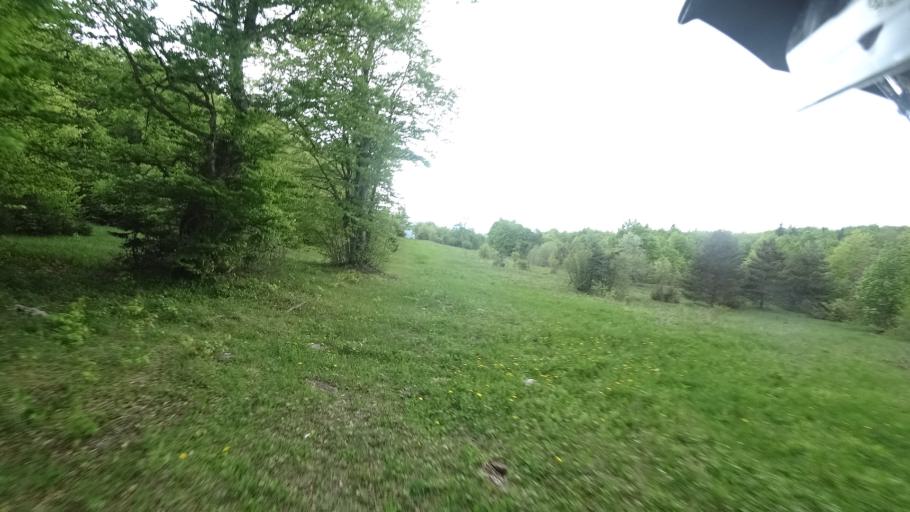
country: HR
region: Karlovacka
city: Plaski
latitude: 44.9092
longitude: 15.4210
